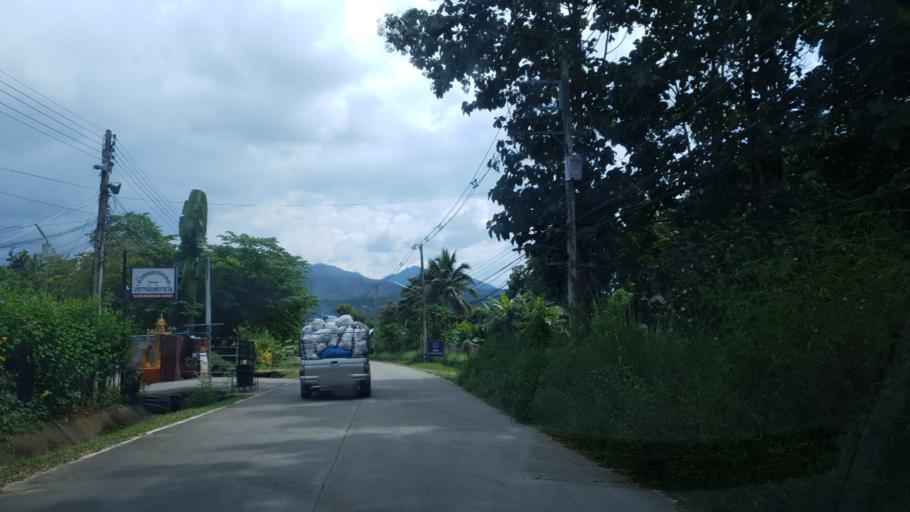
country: TH
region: Mae Hong Son
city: Khun Yuam
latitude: 18.8175
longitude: 97.9325
